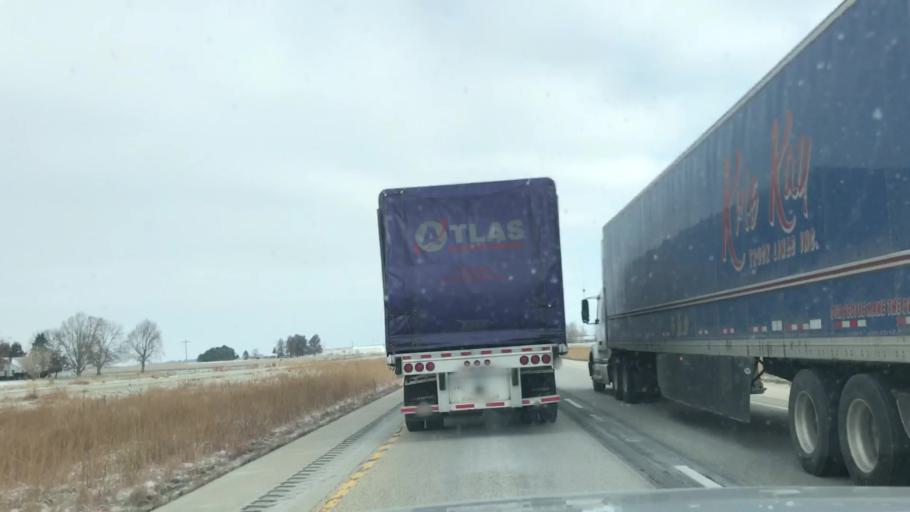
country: US
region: Illinois
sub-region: Sangamon County
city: Divernon
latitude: 39.5173
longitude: -89.6454
